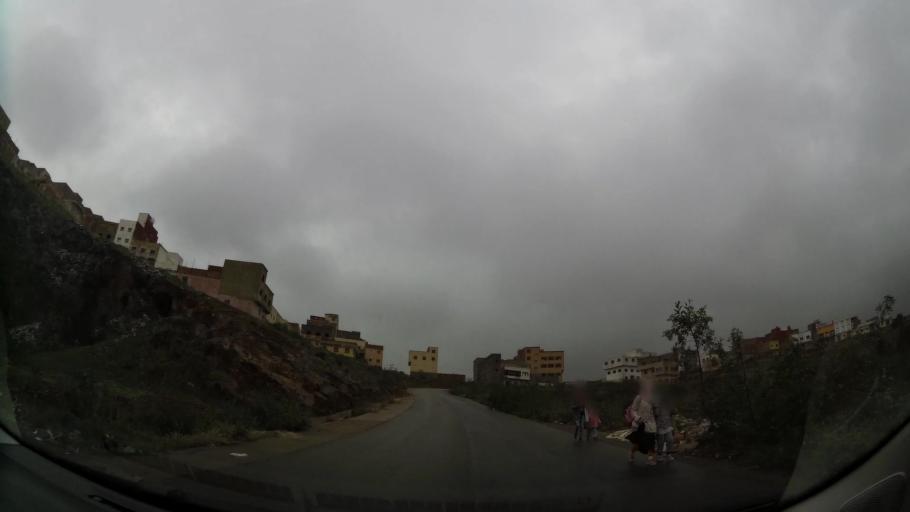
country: MA
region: Oriental
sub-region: Nador
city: Nador
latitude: 35.1860
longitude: -2.9370
